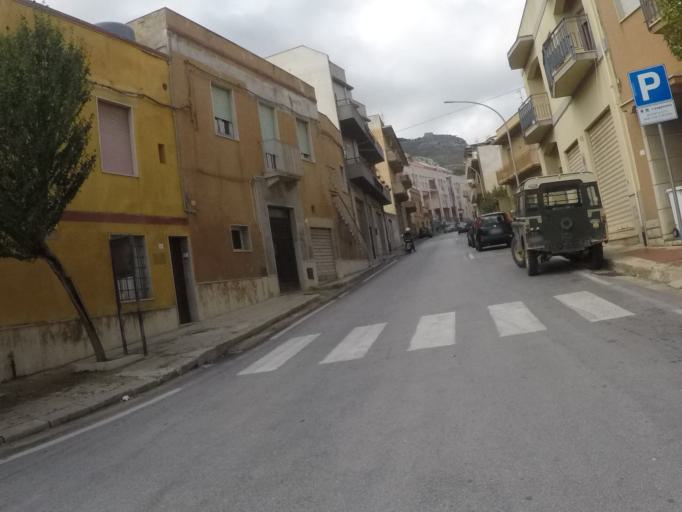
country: IT
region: Sicily
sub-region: Trapani
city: Valderice
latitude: 38.0370
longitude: 12.6123
